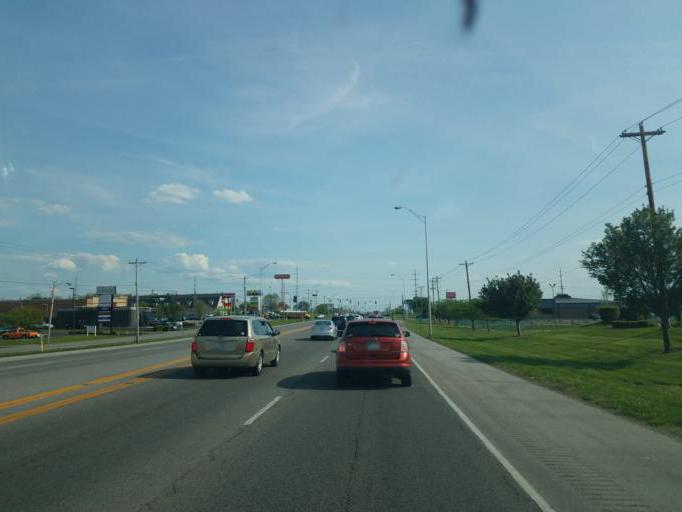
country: US
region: Kentucky
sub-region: Warren County
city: Bowling Green
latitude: 36.9476
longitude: -86.4240
